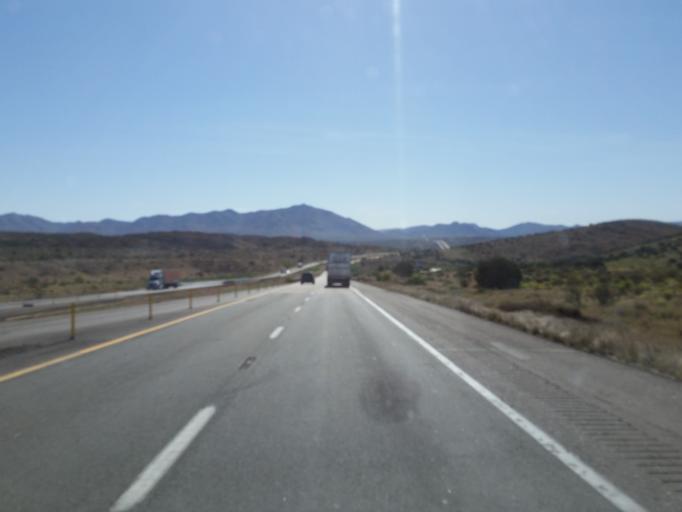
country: US
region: Arizona
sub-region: Mohave County
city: New Kingman-Butler
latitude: 35.1614
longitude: -113.6726
